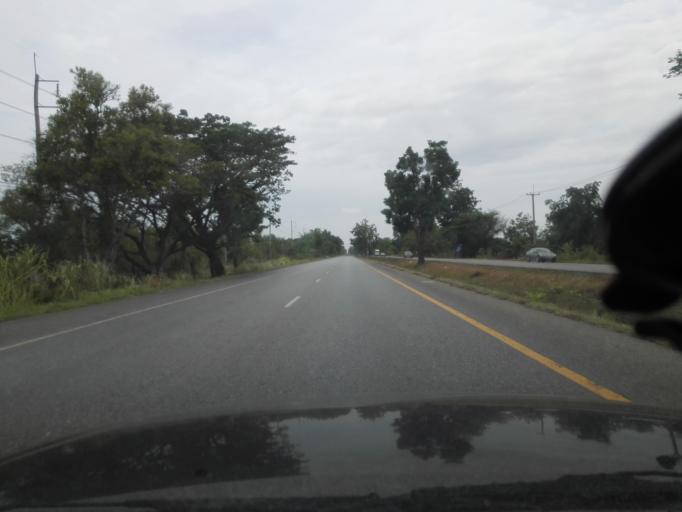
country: TH
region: Kamphaeng Phet
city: Khlong Khlung
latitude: 16.1161
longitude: 99.7194
